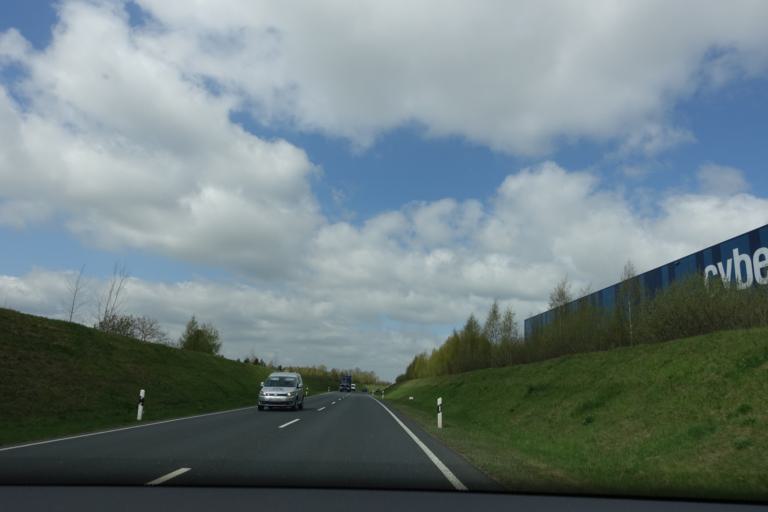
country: DE
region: Saxony
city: Nossen
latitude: 51.0264
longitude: 13.2998
